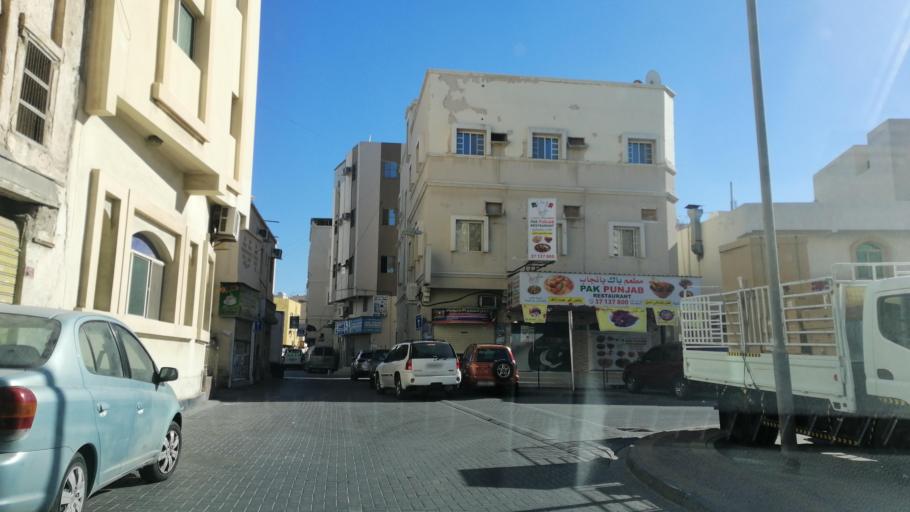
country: BH
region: Muharraq
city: Al Hadd
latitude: 26.2407
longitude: 50.6532
